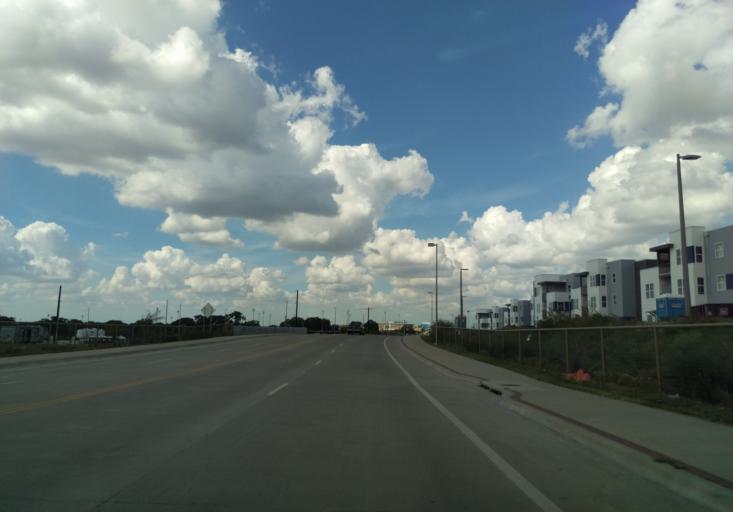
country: US
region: Texas
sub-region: Brazos County
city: College Station
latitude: 30.5960
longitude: -96.3414
